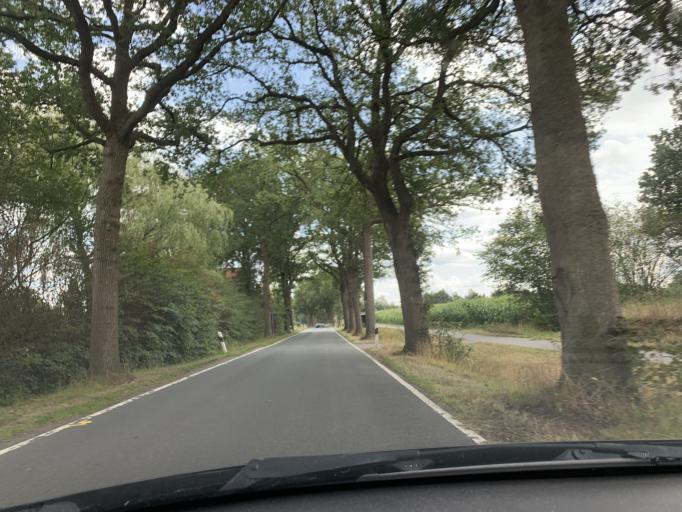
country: DE
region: Lower Saxony
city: Apen
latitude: 53.2517
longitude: 7.8536
